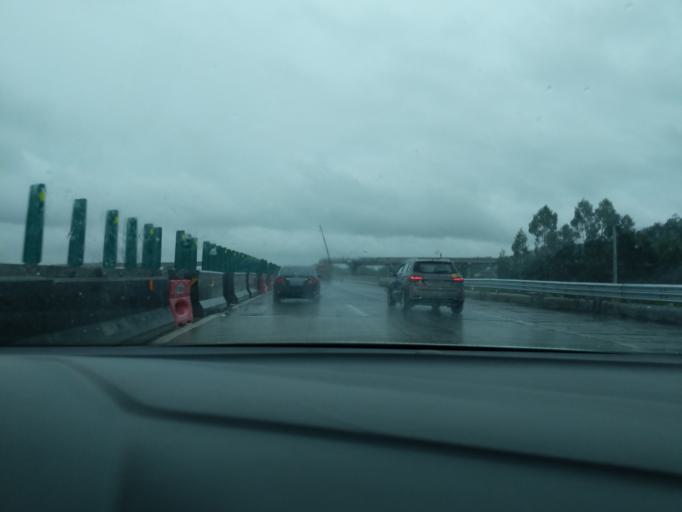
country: CN
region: Guangdong
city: Yueshan
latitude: 22.4635
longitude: 112.7128
